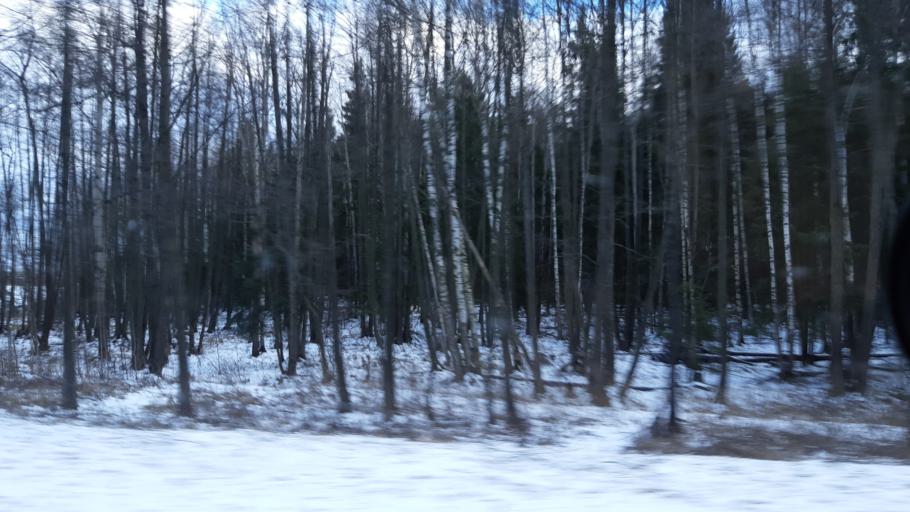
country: RU
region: Moskovskaya
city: Noginsk-9
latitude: 55.9810
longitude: 38.5441
